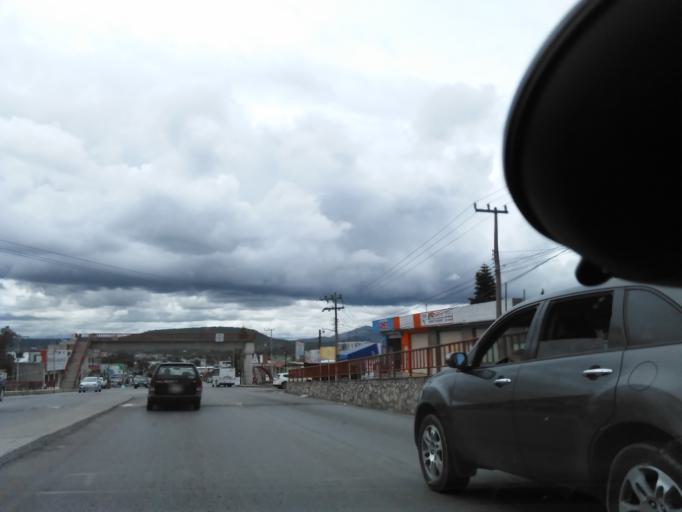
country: MX
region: Hidalgo
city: El Llano
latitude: 20.0557
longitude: -99.3218
